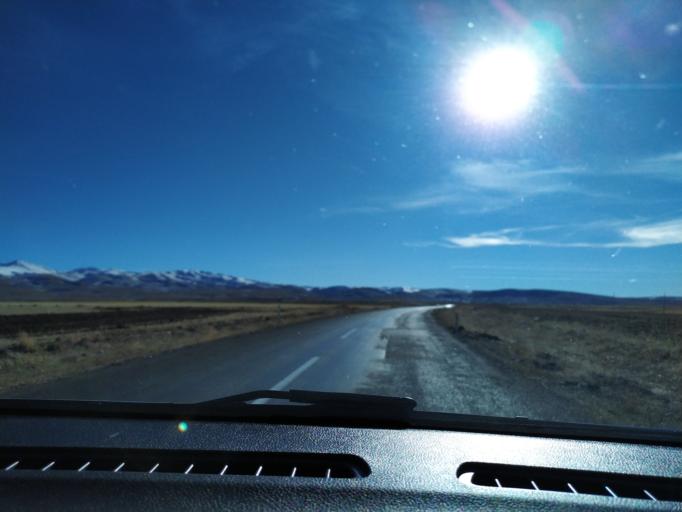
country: TR
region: Kayseri
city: Orensehir
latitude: 38.8837
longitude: 36.7278
